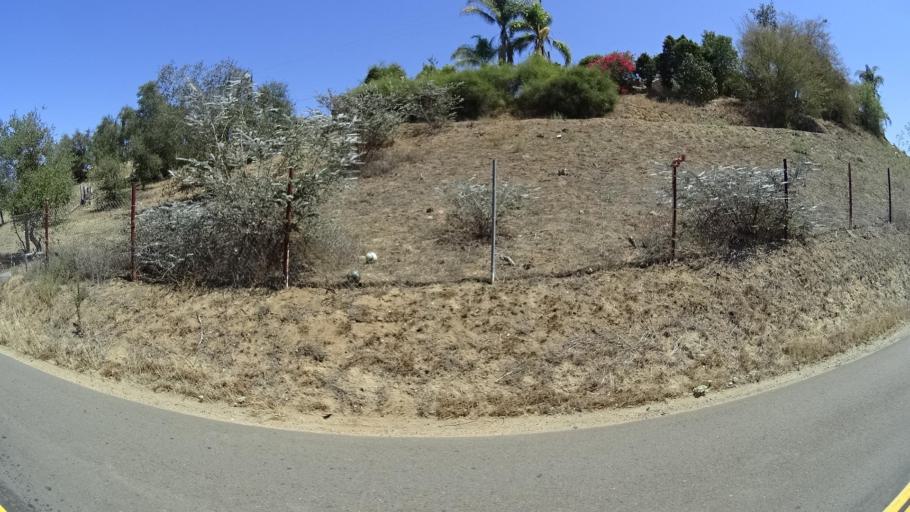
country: US
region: California
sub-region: San Diego County
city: Rainbow
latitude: 33.4059
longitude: -117.1449
